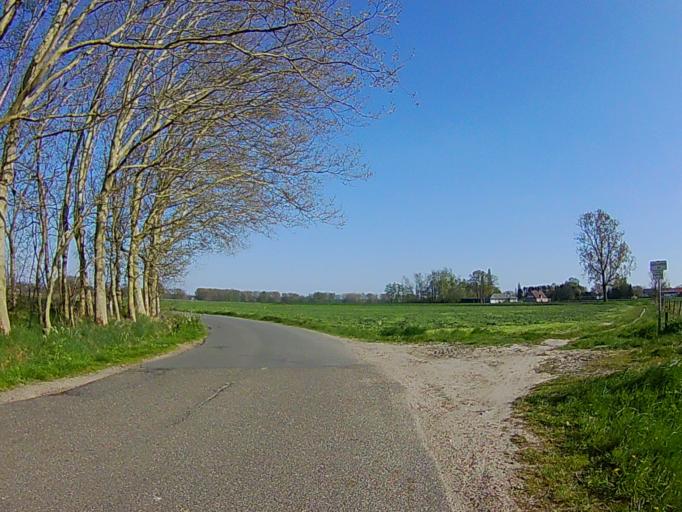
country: BE
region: Flanders
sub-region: Provincie Antwerpen
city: Hoogstraten
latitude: 51.3851
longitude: 4.7666
